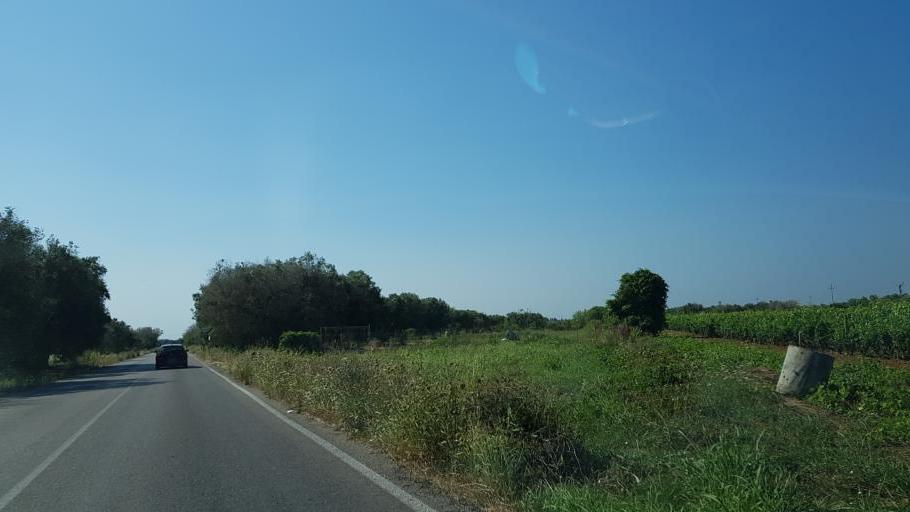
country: IT
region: Apulia
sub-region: Provincia di Lecce
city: Guagnano
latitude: 40.4045
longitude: 17.9674
